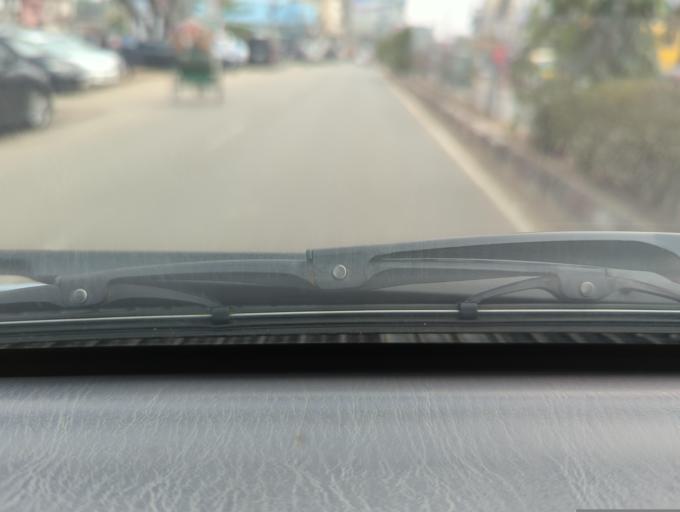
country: BD
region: Sylhet
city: Maulavi Bazar
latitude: 24.4889
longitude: 91.7627
